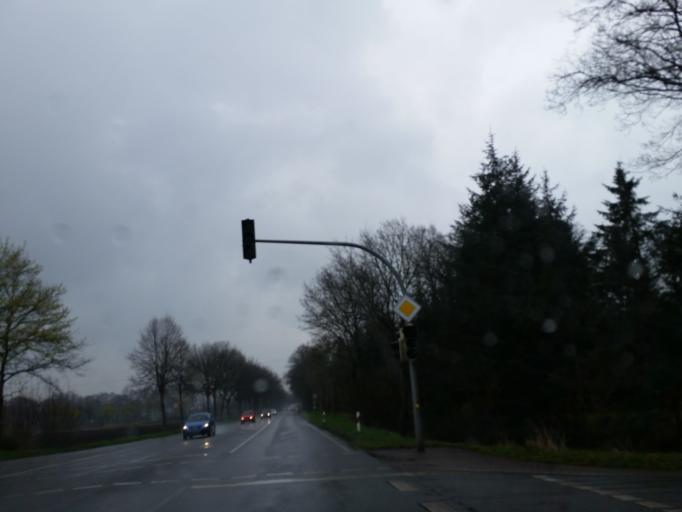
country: DE
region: Lower Saxony
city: Bei der Hohne
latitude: 53.4968
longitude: 9.0940
